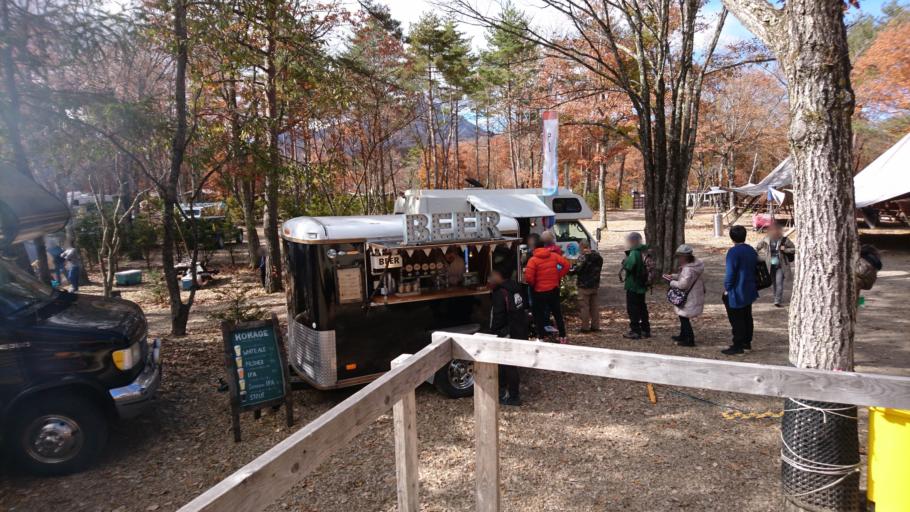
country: JP
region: Nagano
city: Komoro
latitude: 36.3856
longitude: 138.6179
